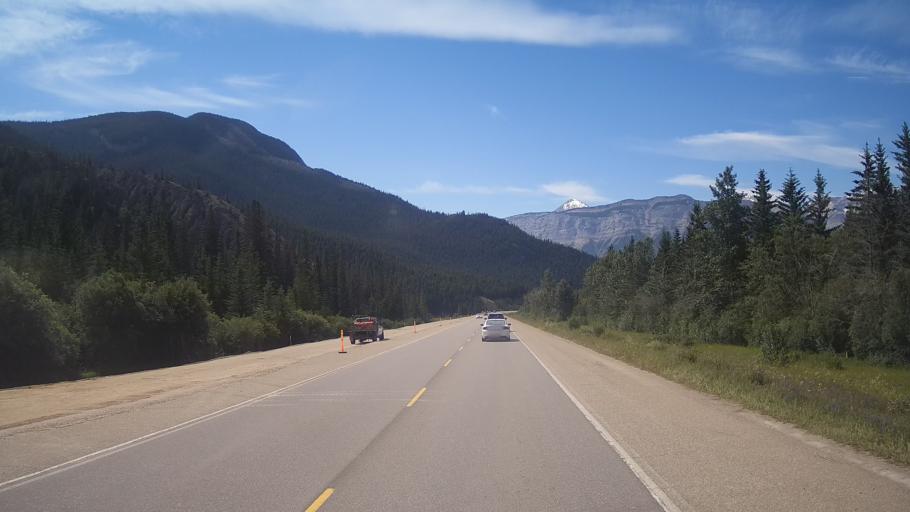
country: CA
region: Alberta
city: Jasper Park Lodge
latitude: 53.0590
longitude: -118.0677
